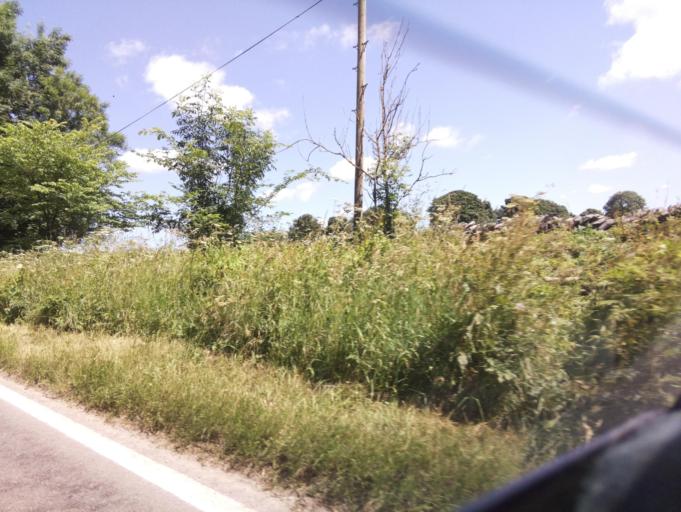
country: GB
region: England
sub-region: Derbyshire
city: Bakewell
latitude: 53.1360
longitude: -1.7534
